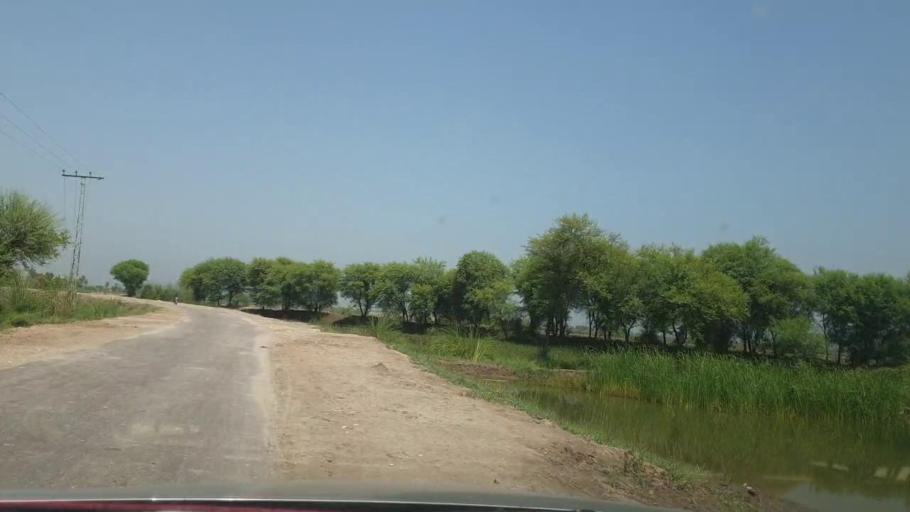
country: PK
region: Sindh
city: Warah
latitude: 27.4707
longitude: 67.7636
